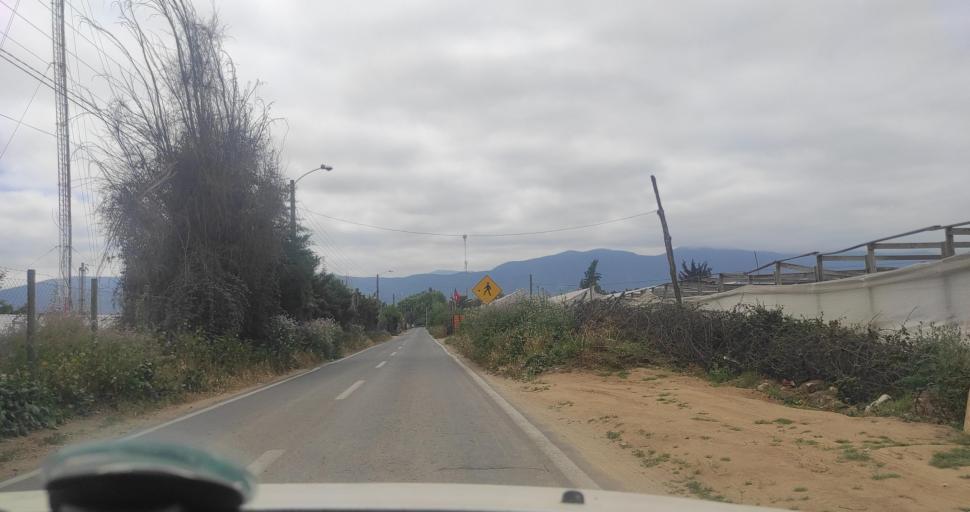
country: CL
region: Valparaiso
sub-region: Provincia de Marga Marga
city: Limache
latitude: -33.0327
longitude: -71.2408
